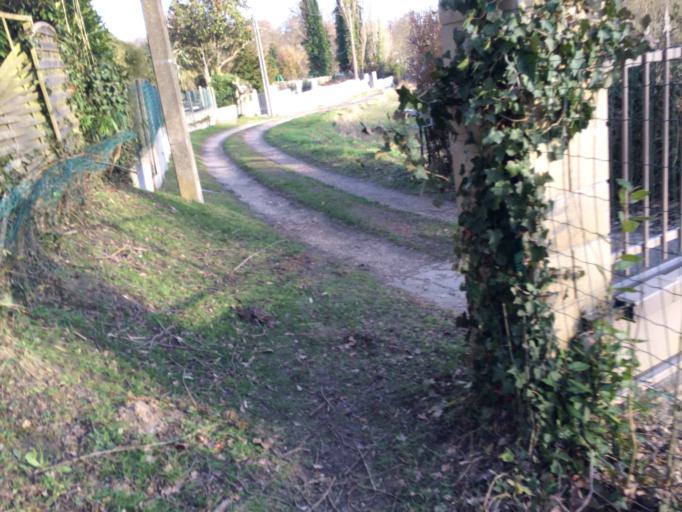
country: FR
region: Ile-de-France
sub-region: Departement de l'Essonne
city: Champlan
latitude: 48.7074
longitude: 2.2672
